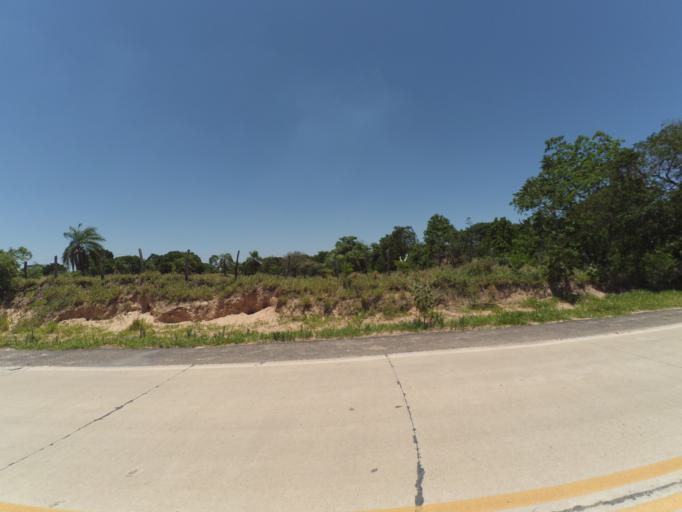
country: BO
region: Santa Cruz
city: Santa Rita
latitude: -17.8453
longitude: -63.3012
